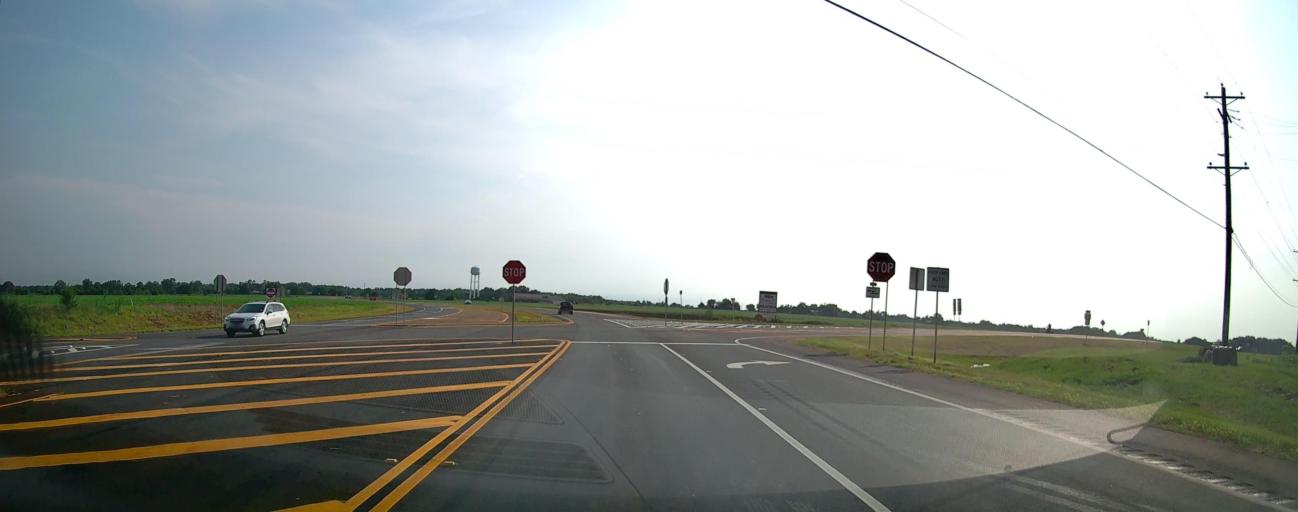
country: US
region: Georgia
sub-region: Peach County
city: Fort Valley
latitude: 32.5774
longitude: -83.9079
